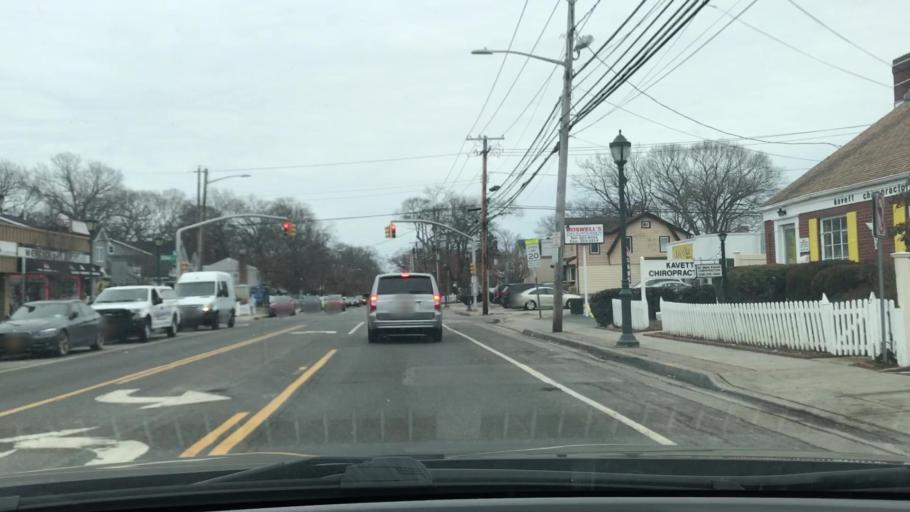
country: US
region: New York
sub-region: Nassau County
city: Merrick
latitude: 40.6737
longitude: -73.5564
